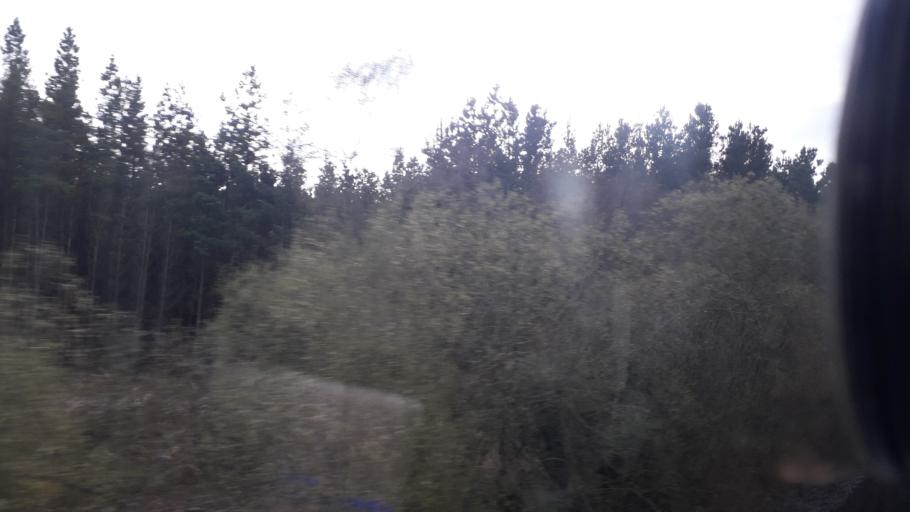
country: IE
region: Leinster
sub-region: An Iarmhi
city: Rochfortbridge
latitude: 53.4986
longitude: -7.2499
